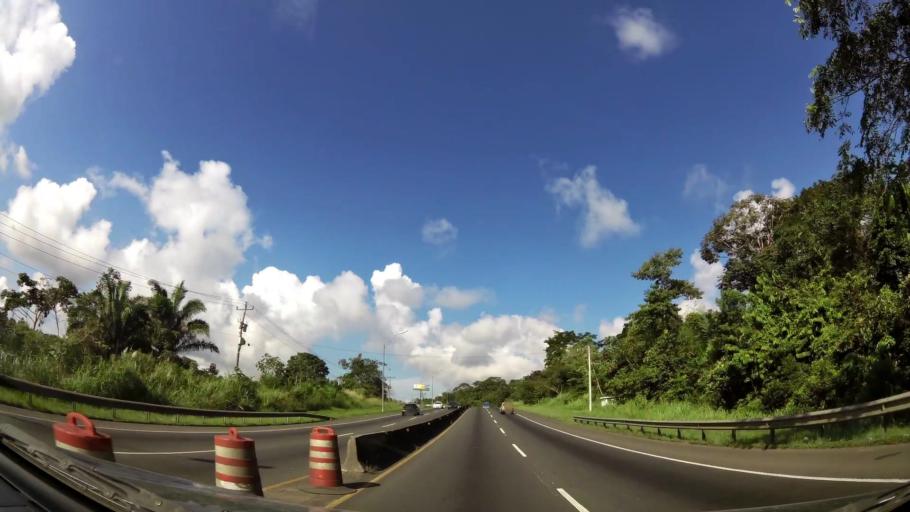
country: PA
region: Panama
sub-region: Distrito Arraijan
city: Arraijan
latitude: 8.9551
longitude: -79.6448
